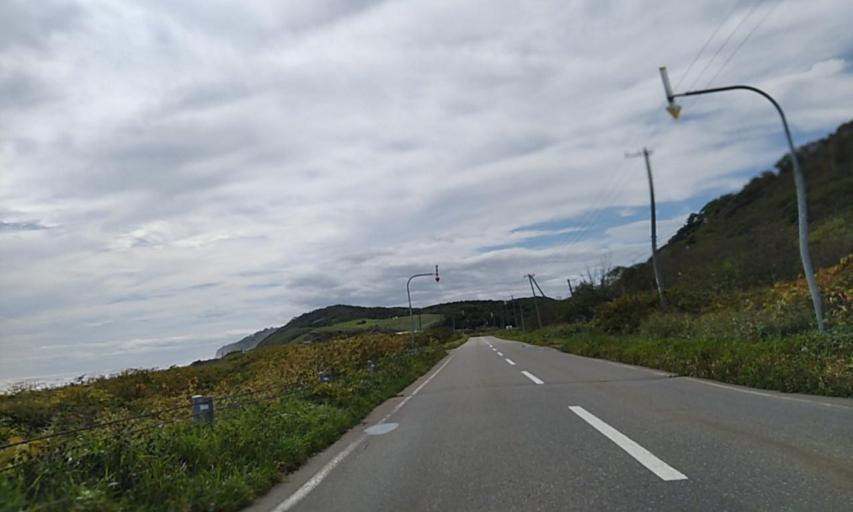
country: JP
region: Hokkaido
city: Obihiro
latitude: 42.7877
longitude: 143.7926
